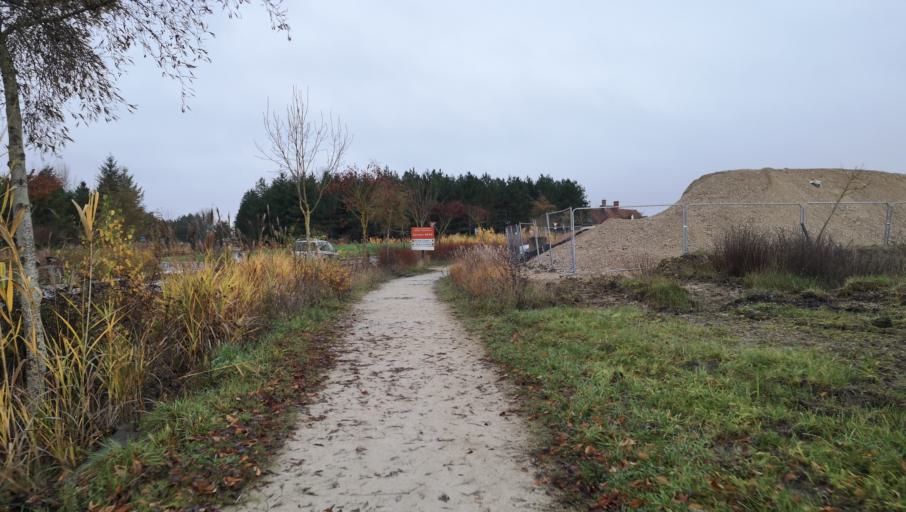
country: FR
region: Centre
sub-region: Departement du Loiret
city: Marigny-les-Usages
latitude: 47.9482
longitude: 2.0097
